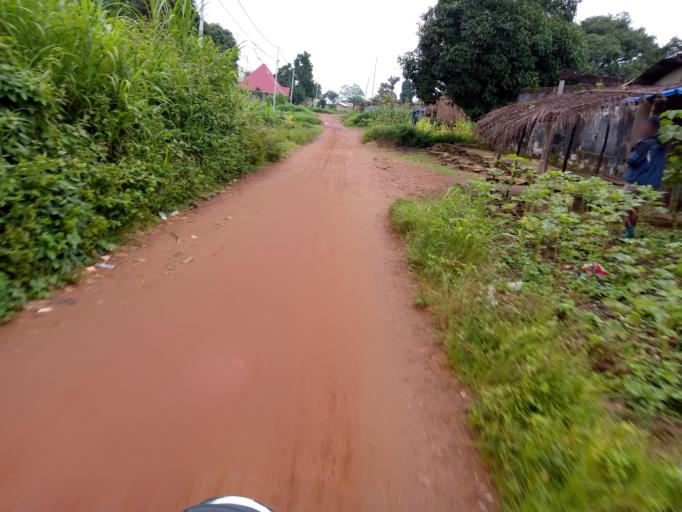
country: SL
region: Eastern Province
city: Buedu
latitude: 8.4649
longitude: -10.3415
